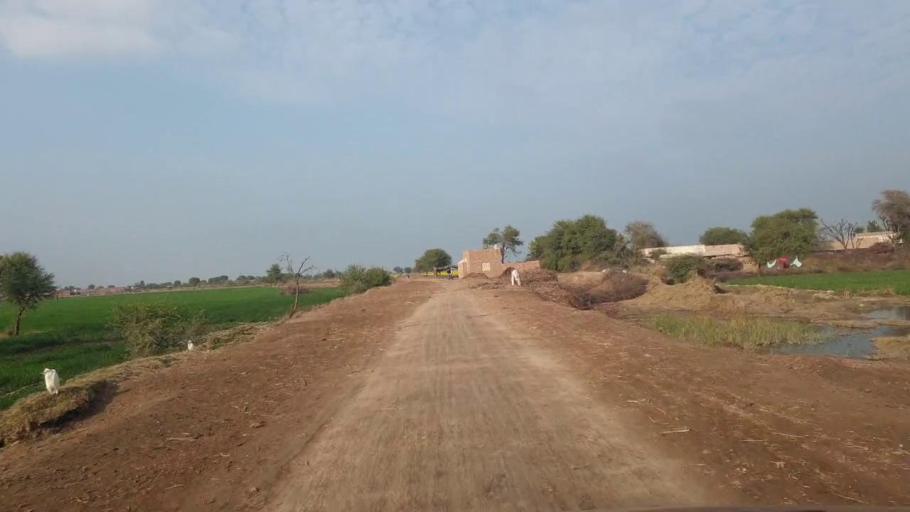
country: PK
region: Sindh
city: Shahdadpur
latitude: 25.8772
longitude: 68.7162
